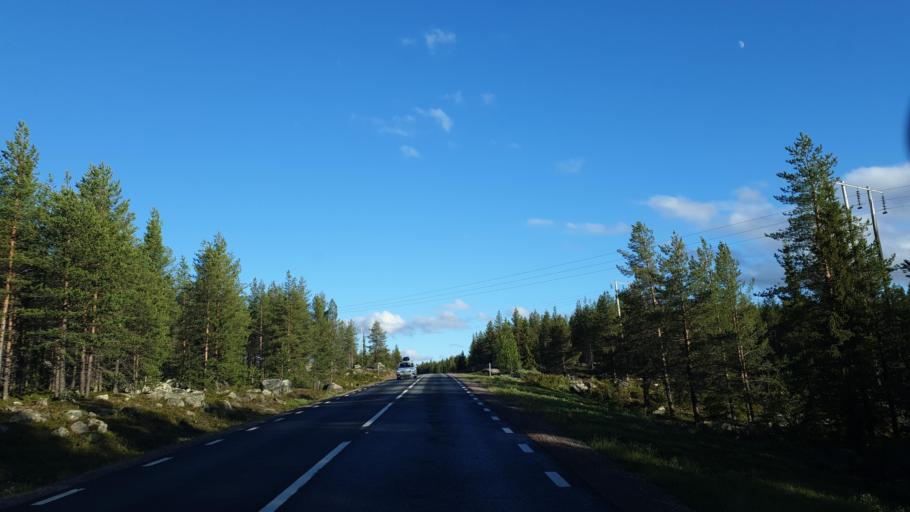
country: SE
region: Norrbotten
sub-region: Arjeplogs Kommun
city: Arjeplog
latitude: 65.9591
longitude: 18.2703
